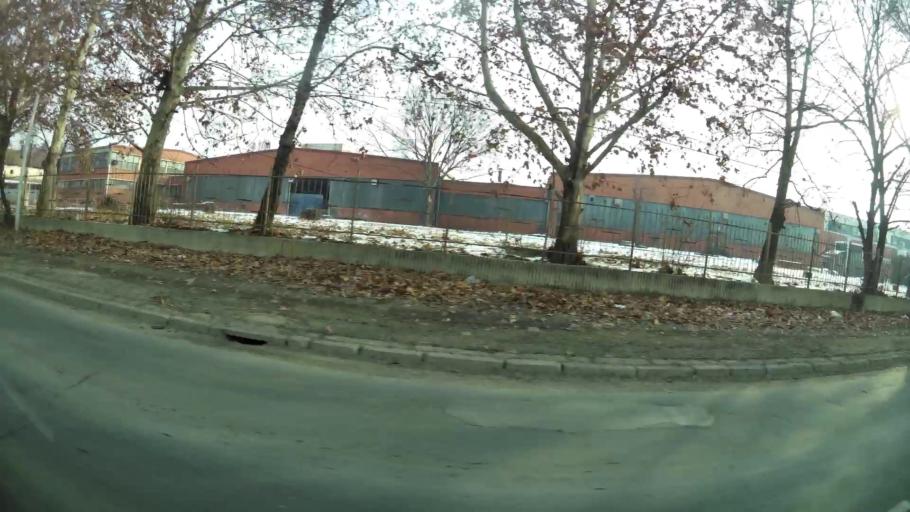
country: MK
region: Cair
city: Cair
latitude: 42.0236
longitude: 21.4302
